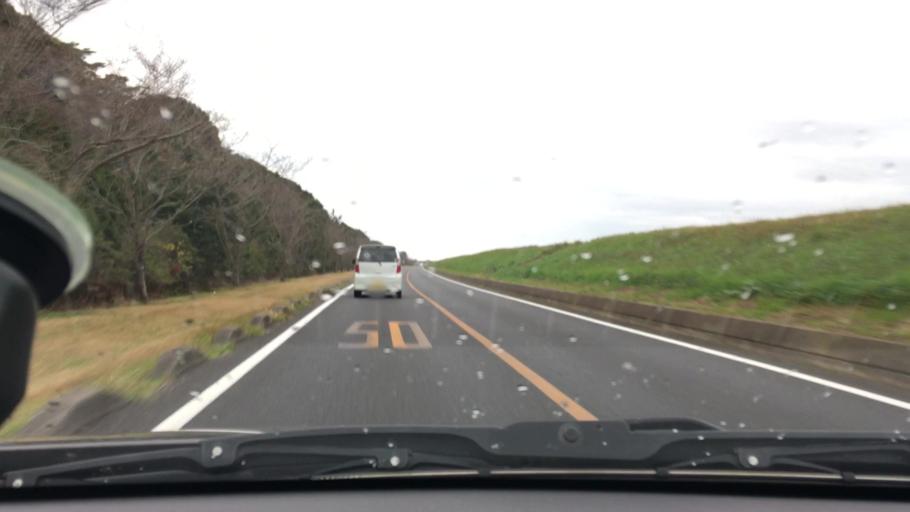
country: JP
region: Chiba
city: Omigawa
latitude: 35.8502
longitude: 140.6865
